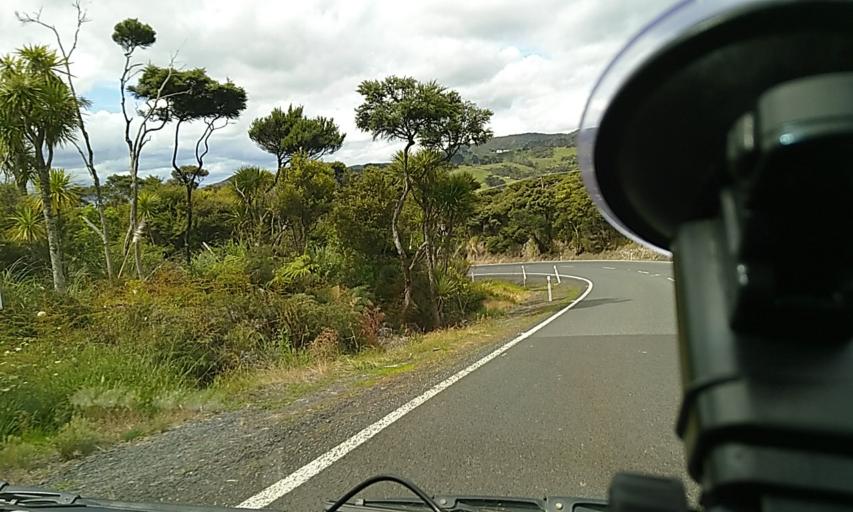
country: NZ
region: Northland
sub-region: Far North District
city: Ahipara
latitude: -35.5395
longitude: 173.3850
